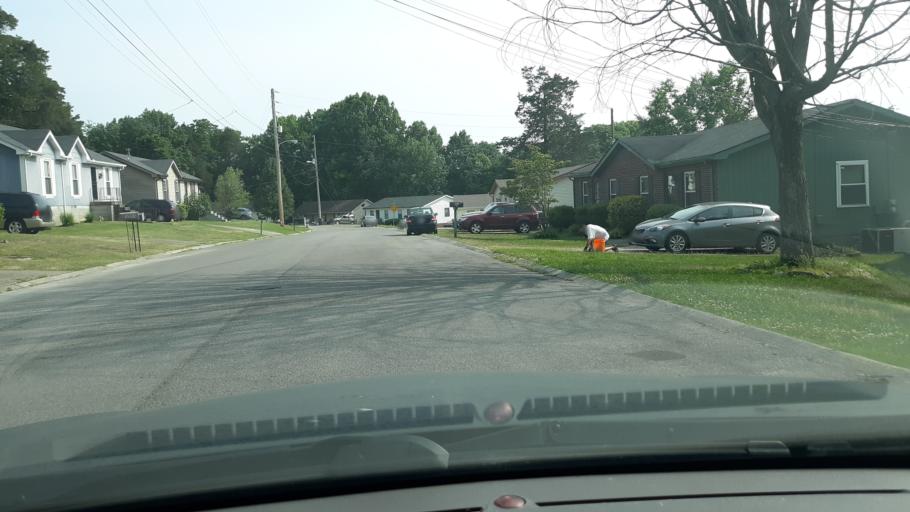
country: US
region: Tennessee
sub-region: Davidson County
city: Lakewood
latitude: 36.1793
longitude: -86.6112
